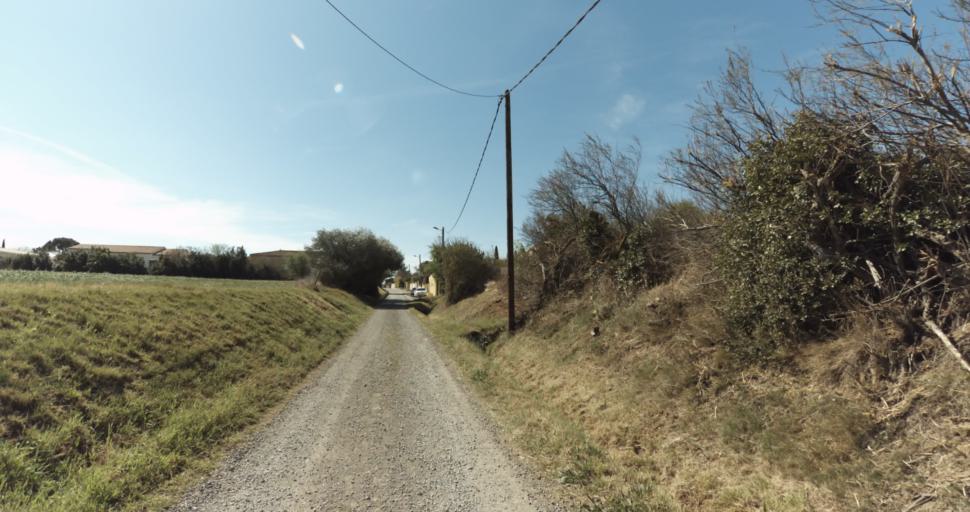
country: FR
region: Languedoc-Roussillon
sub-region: Departement de l'Herault
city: Marseillan
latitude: 43.3634
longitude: 3.5293
